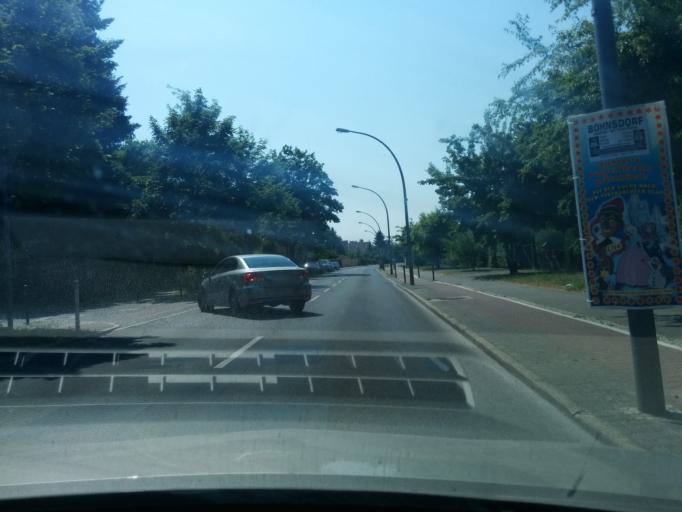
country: DE
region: Berlin
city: Bohnsdorf
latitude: 52.3990
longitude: 13.5749
